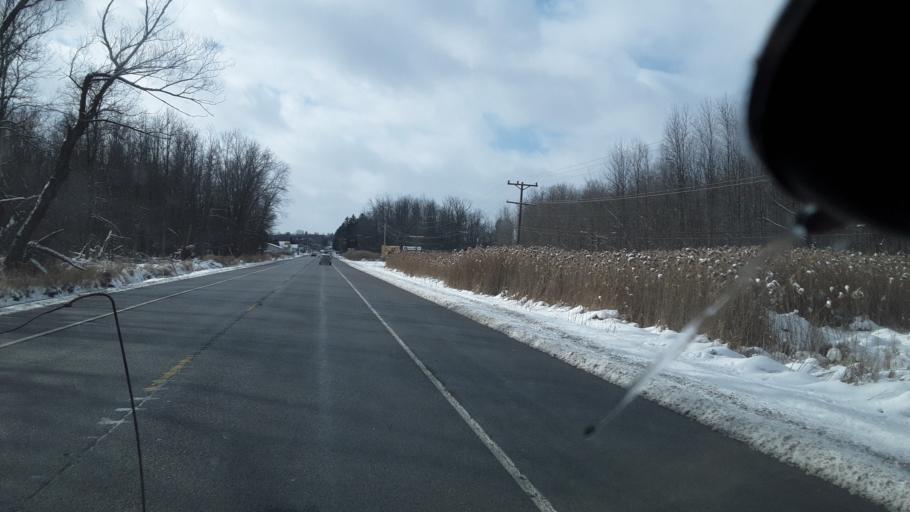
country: US
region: New York
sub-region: Wayne County
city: Newark
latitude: 43.0503
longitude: -77.0664
